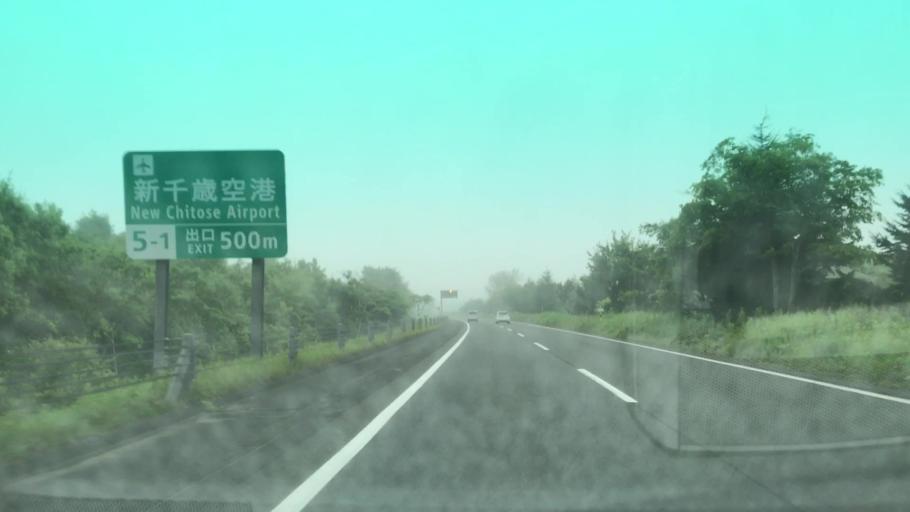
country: JP
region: Hokkaido
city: Chitose
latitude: 42.7848
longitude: 141.6268
